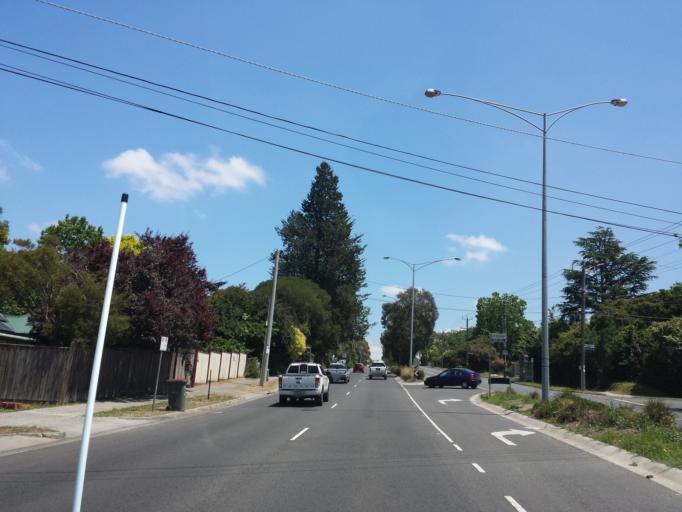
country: AU
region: Victoria
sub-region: Maroondah
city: Croydon North
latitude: -37.8005
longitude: 145.2960
